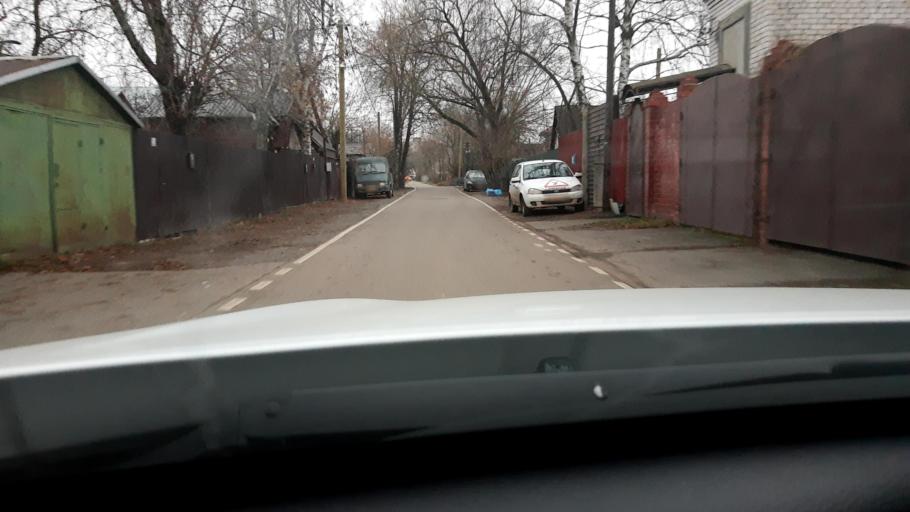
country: RU
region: Moscow
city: Zhulebino
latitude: 55.7155
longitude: 37.8485
